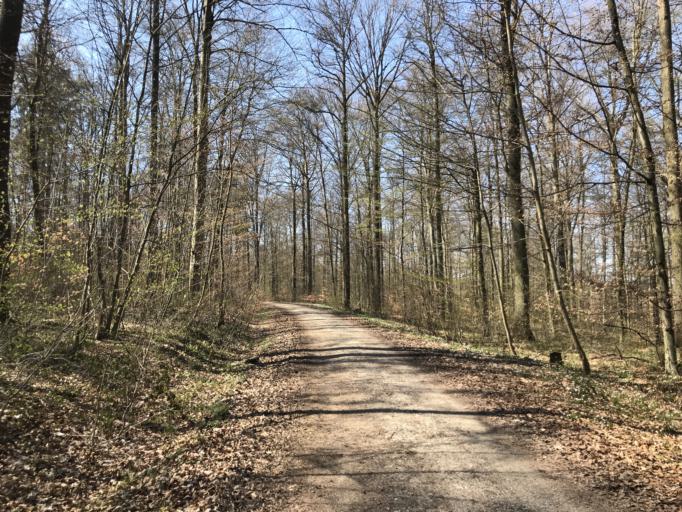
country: DE
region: Baden-Wuerttemberg
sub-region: Regierungsbezirk Stuttgart
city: Unterensingen
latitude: 48.6560
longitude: 9.3346
